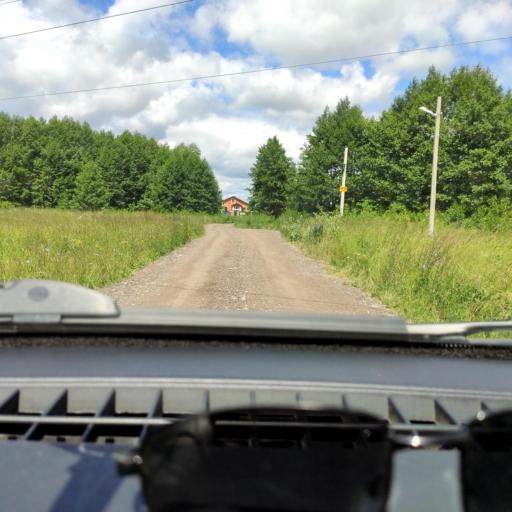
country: RU
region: Bashkortostan
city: Kabakovo
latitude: 54.6718
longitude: 56.0966
